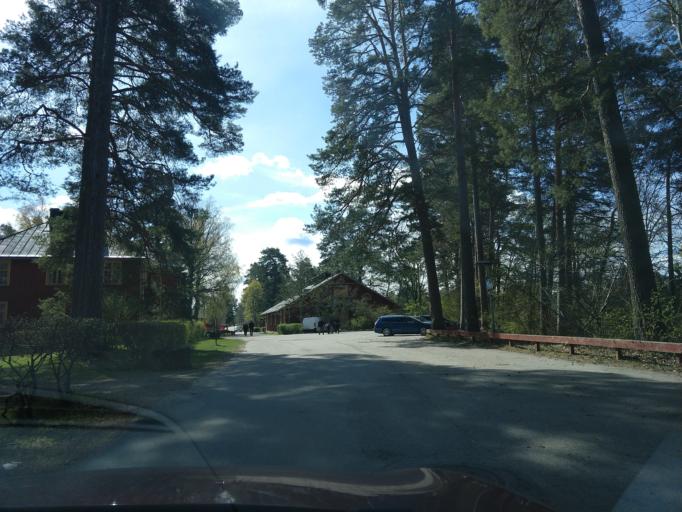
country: SE
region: Uppsala
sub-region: Alvkarleby Kommun
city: AElvkarleby
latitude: 60.5635
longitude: 17.4362
